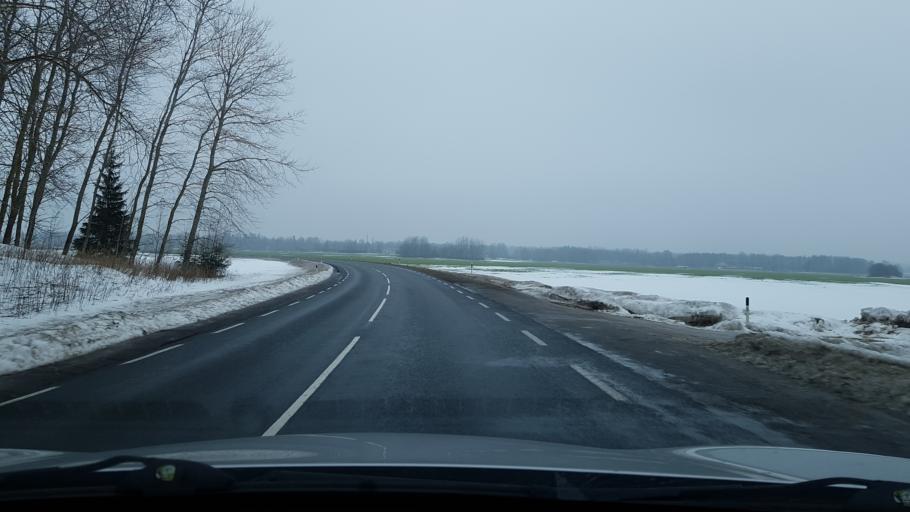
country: EE
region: Valgamaa
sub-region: Torva linn
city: Torva
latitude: 58.2072
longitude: 25.9483
